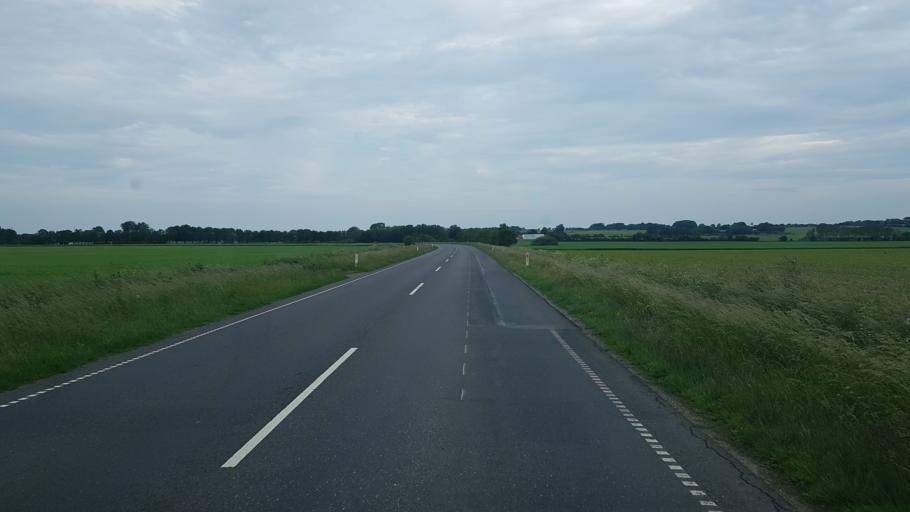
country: DK
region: South Denmark
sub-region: Vejen Kommune
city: Rodding
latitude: 55.4055
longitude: 9.0329
